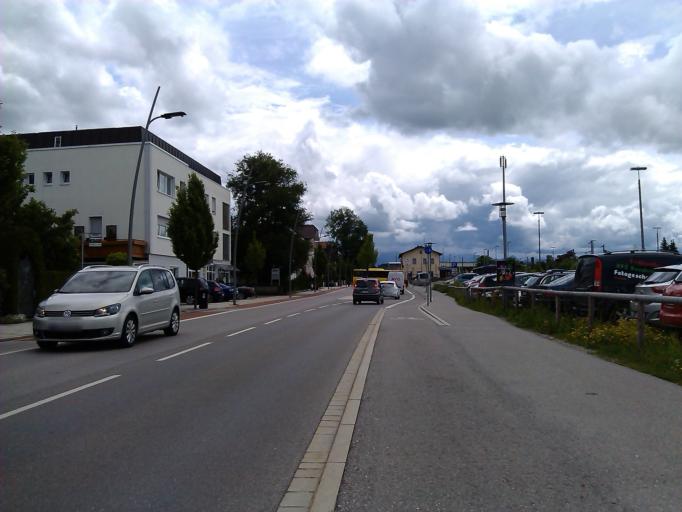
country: DE
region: Bavaria
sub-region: Swabia
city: Marktoberdorf
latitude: 47.7812
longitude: 10.6149
